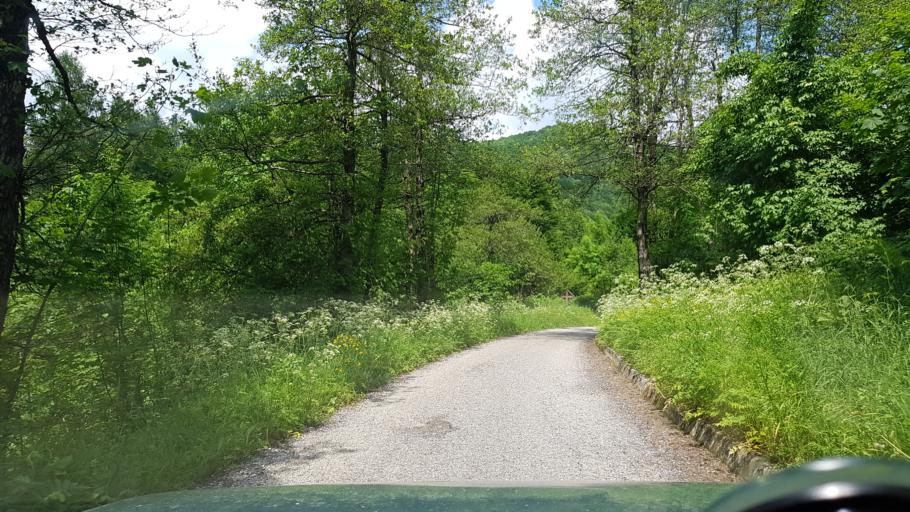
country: IT
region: Friuli Venezia Giulia
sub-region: Provincia di Udine
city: Pulfero
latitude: 46.1988
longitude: 13.4342
